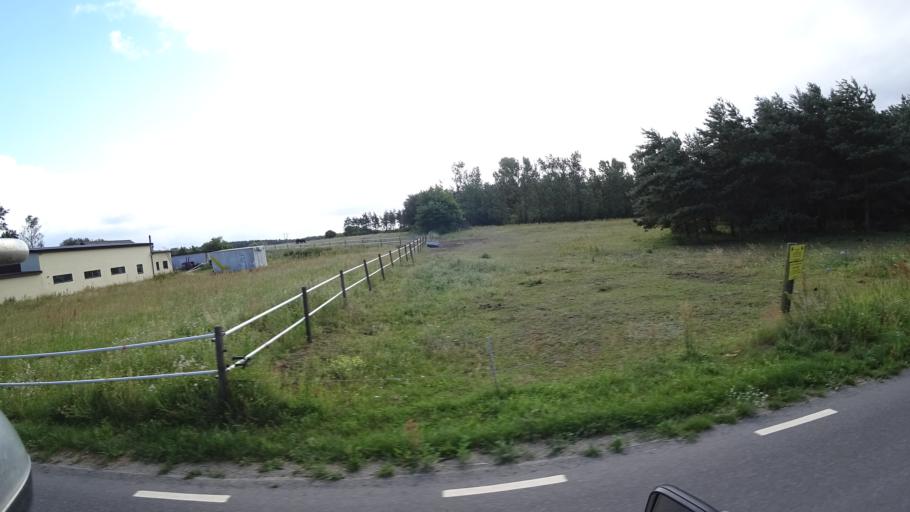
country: SE
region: Skane
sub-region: Kristianstads Kommun
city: Norra Asum
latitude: 55.9616
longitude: 14.1203
